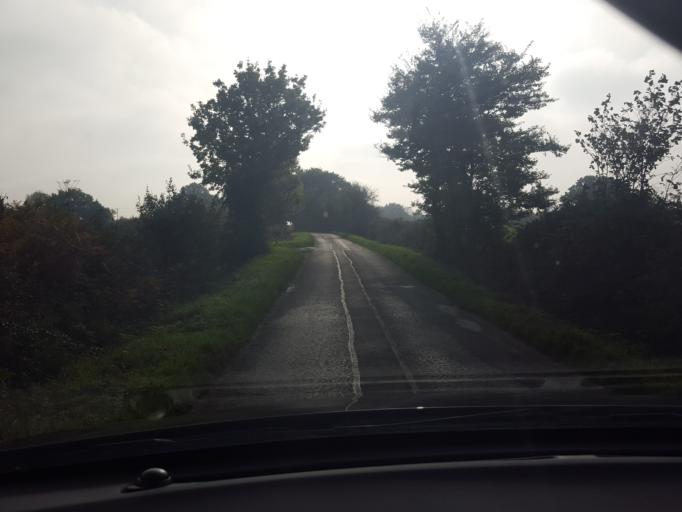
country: GB
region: England
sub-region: Essex
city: Mistley
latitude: 51.9256
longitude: 1.1486
